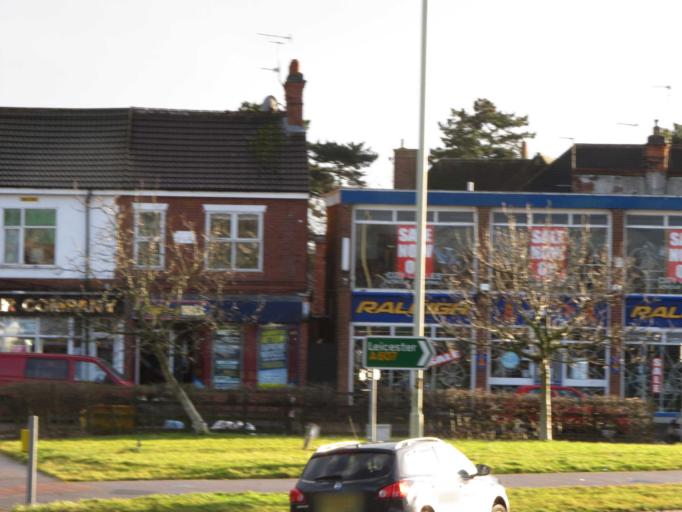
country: GB
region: England
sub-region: Leicestershire
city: Syston
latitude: 52.6740
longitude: -1.1025
